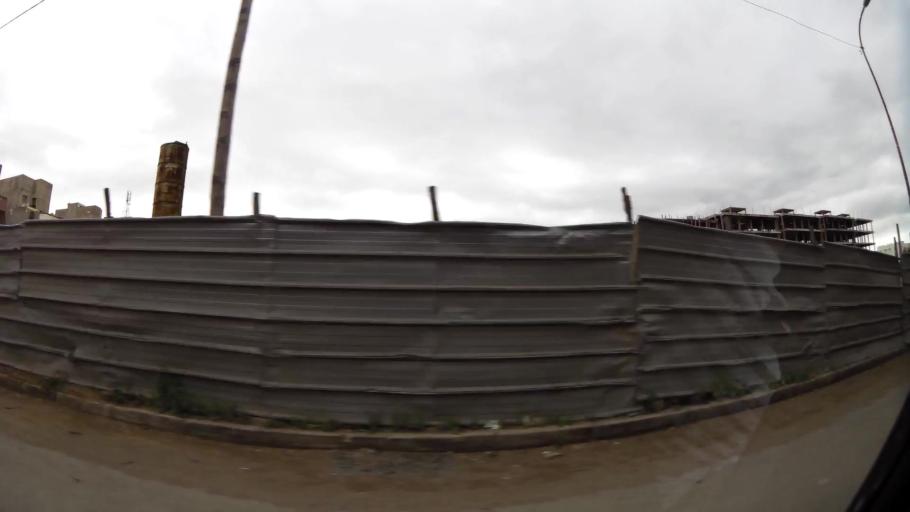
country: MA
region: Grand Casablanca
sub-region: Mediouna
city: Tit Mellil
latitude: 33.5571
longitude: -7.5322
